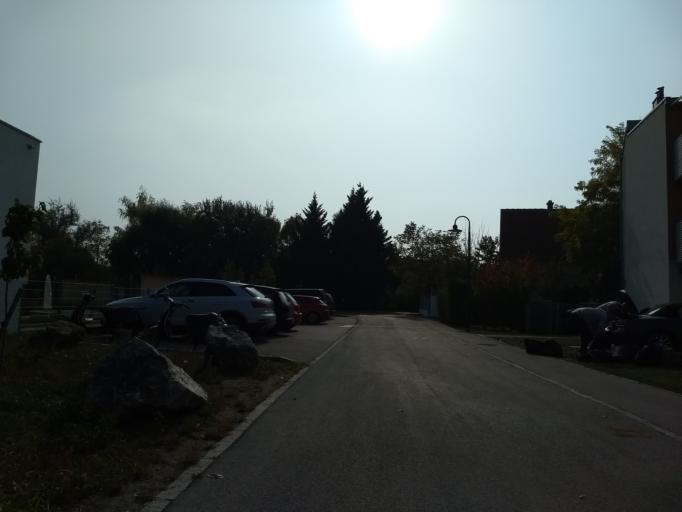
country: AT
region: Lower Austria
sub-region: Politischer Bezirk Modling
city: Brunn am Gebirge
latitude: 48.1261
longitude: 16.2909
